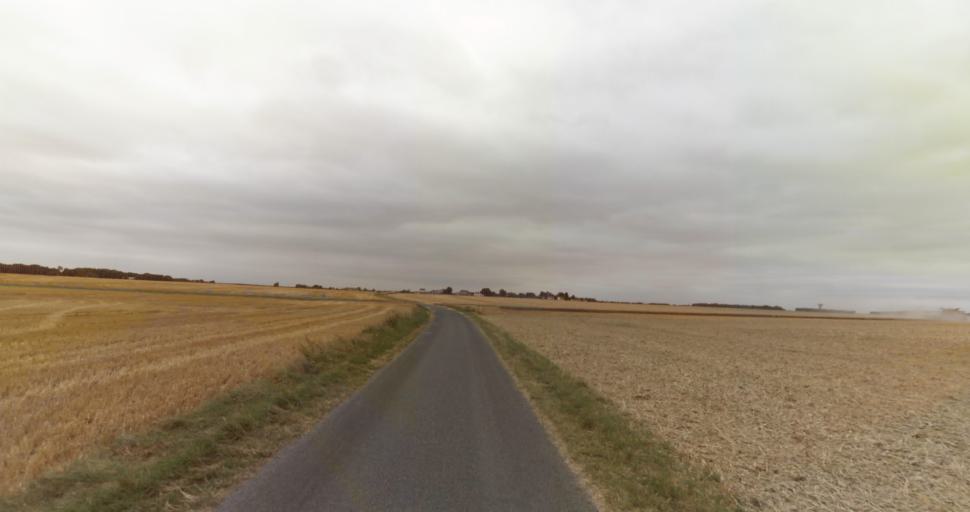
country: FR
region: Haute-Normandie
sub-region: Departement de l'Eure
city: La Couture-Boussey
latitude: 48.9378
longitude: 1.3333
